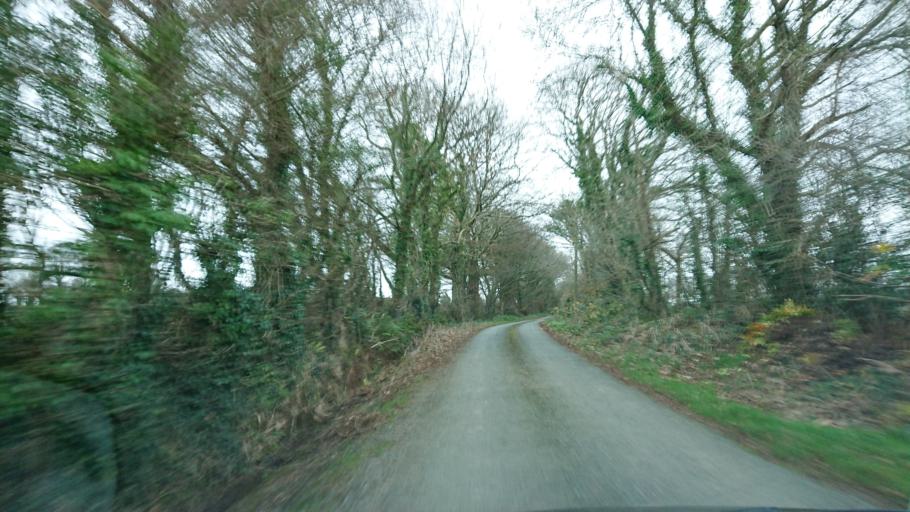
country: IE
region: Munster
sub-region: Waterford
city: Dunmore East
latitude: 52.1937
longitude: -7.0360
